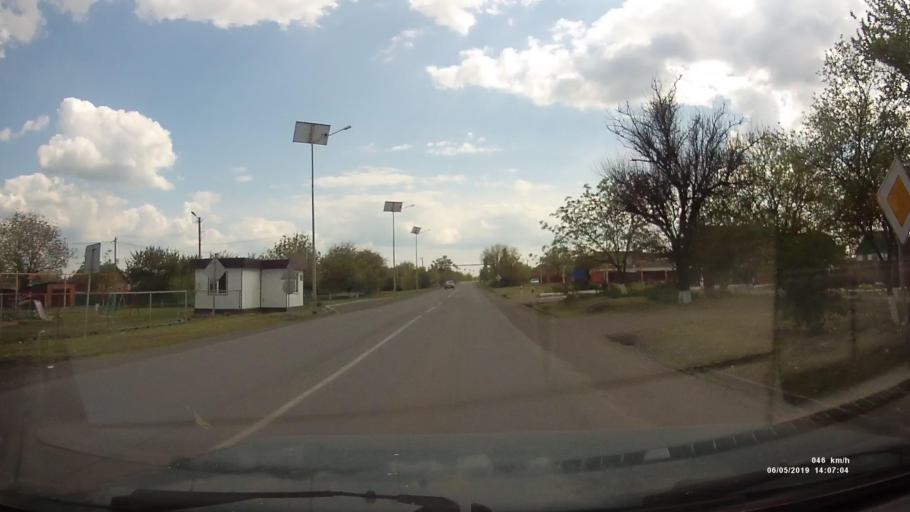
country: RU
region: Rostov
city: Shakhty
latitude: 47.6839
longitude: 40.3029
